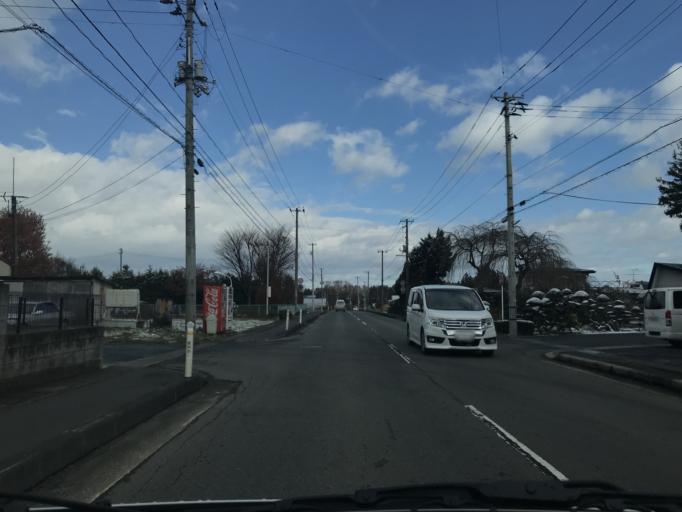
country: JP
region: Iwate
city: Mizusawa
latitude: 39.1176
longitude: 141.1379
